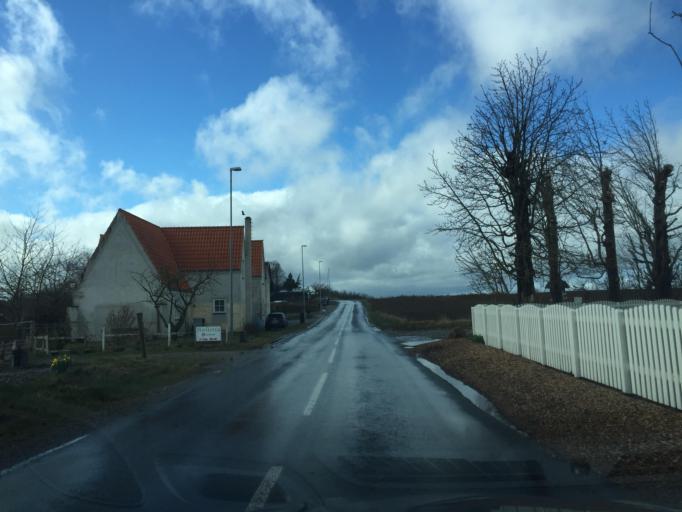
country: DK
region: South Denmark
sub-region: Odense Kommune
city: Odense
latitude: 55.4433
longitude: 10.3381
